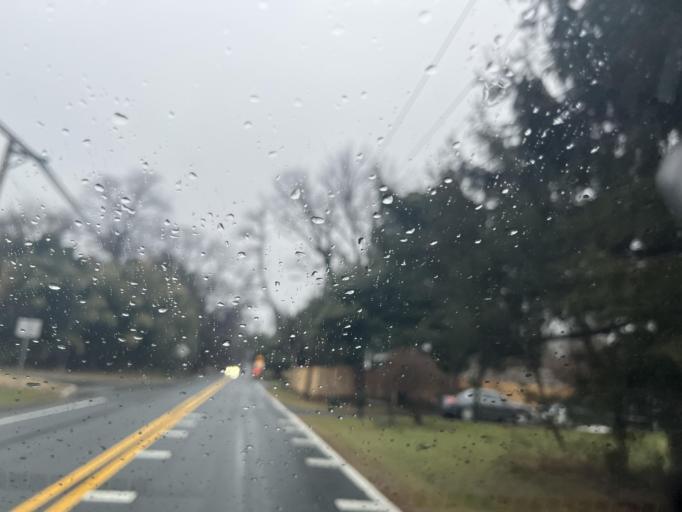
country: US
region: Maryland
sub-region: Montgomery County
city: Germantown
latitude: 39.1877
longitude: -77.3185
